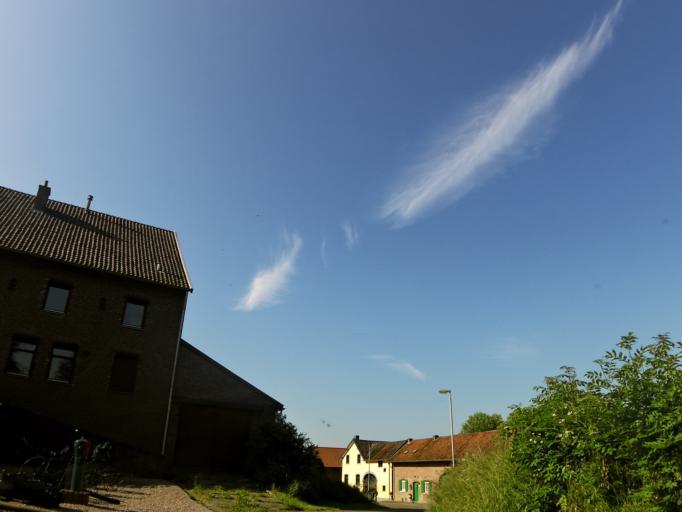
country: NL
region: Limburg
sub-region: Valkenburg aan de Geul
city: Schin op Geul
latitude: 50.8464
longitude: 5.8911
